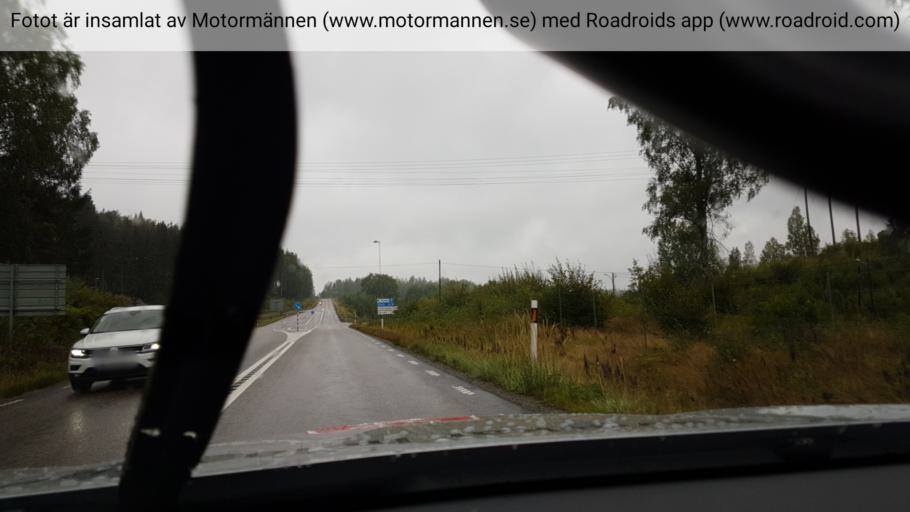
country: SE
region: Vaestra Goetaland
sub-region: Bengtsfors Kommun
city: Billingsfors
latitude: 59.0153
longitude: 12.2725
